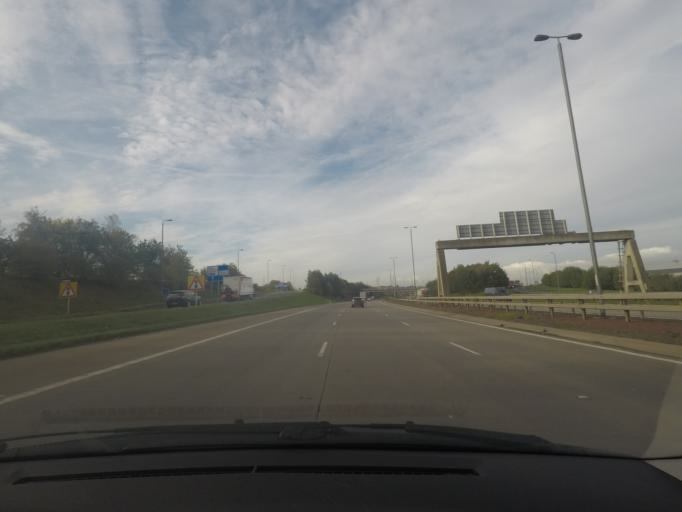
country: GB
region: England
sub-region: City and Borough of Leeds
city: Lofthouse
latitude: 53.7635
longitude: -1.4870
